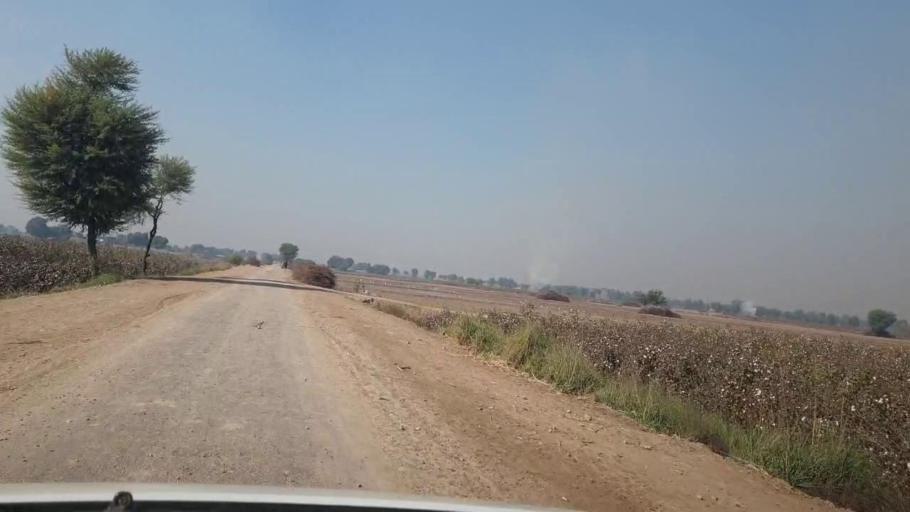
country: PK
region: Sindh
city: Bhan
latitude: 26.6117
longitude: 67.7734
